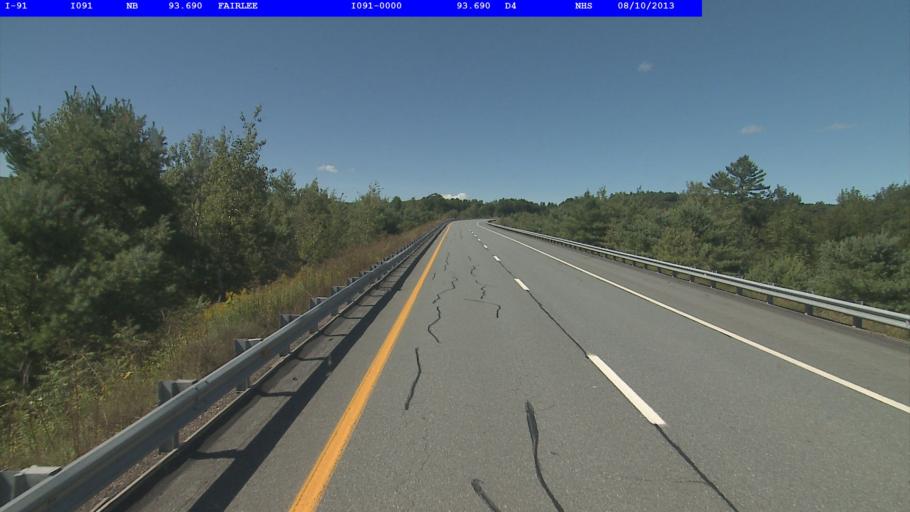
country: US
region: New Hampshire
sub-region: Grafton County
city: Orford
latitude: 43.9287
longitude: -72.1337
